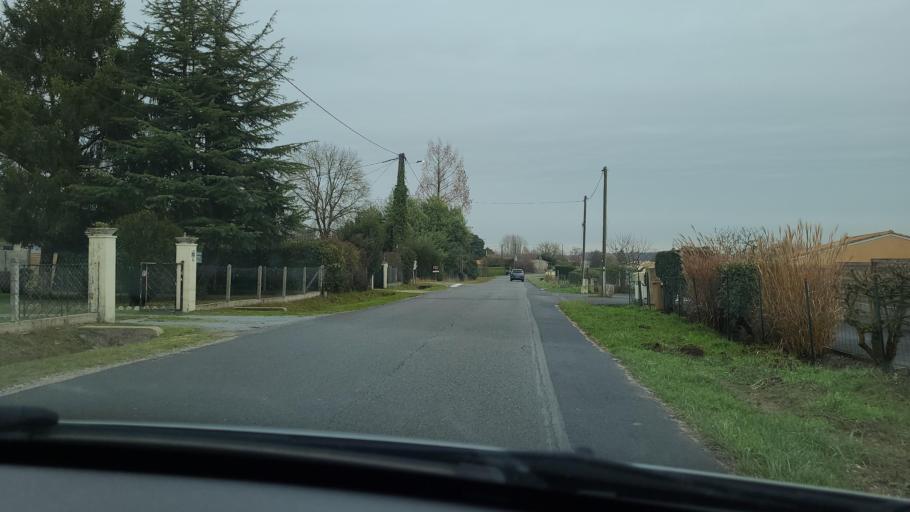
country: FR
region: Aquitaine
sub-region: Departement de la Gironde
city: Pugnac
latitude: 45.0826
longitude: -0.4880
